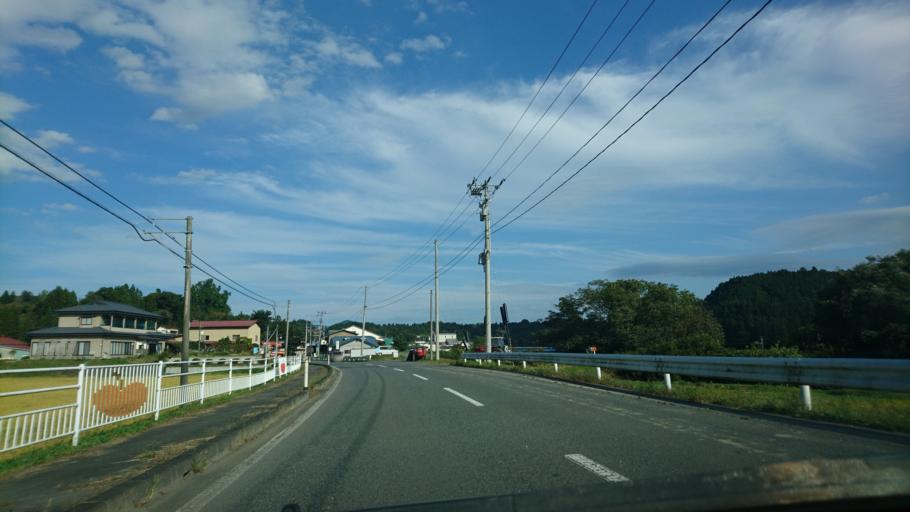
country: JP
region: Iwate
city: Ichinoseki
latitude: 38.8485
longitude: 141.2907
